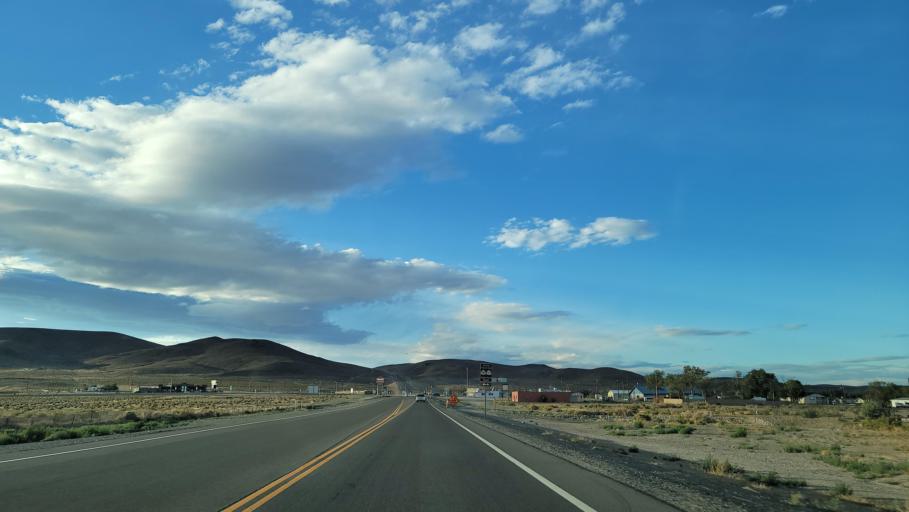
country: US
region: Nevada
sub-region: Lyon County
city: Silver Springs
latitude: 39.4107
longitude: -119.2261
